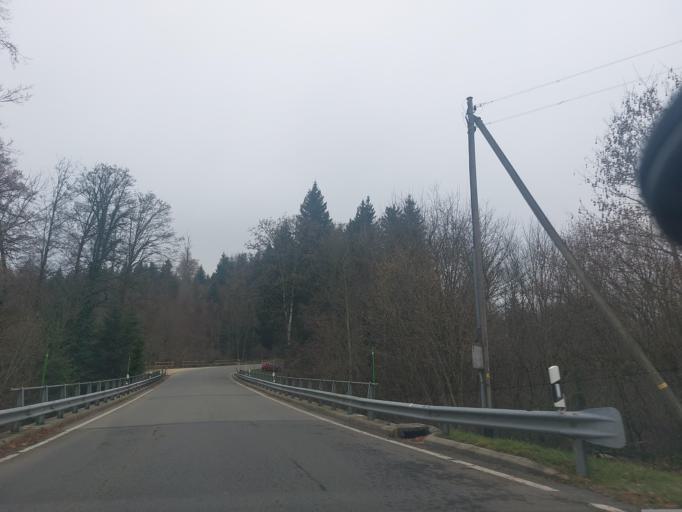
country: CH
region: Vaud
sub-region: Lavaux-Oron District
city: Palezieux
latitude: 46.5455
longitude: 6.8457
